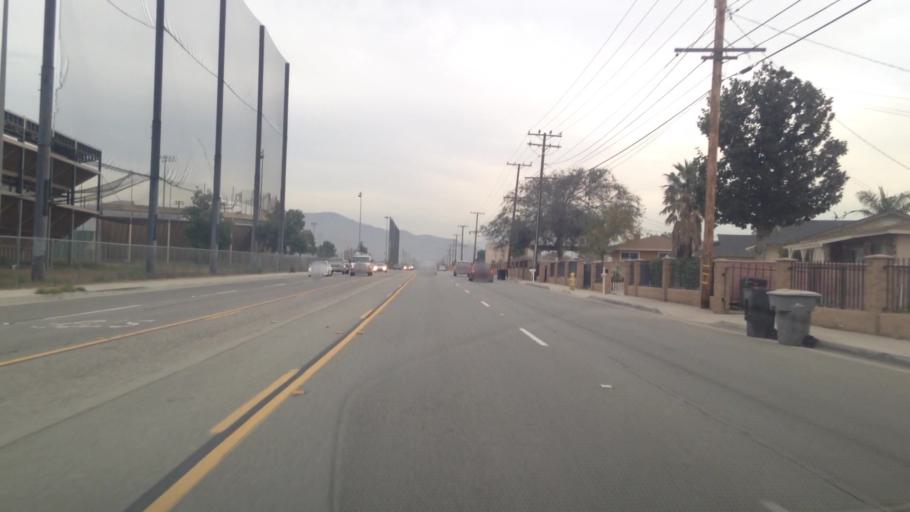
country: US
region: California
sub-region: Riverside County
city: Mira Loma
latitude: 34.0011
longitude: -117.5188
